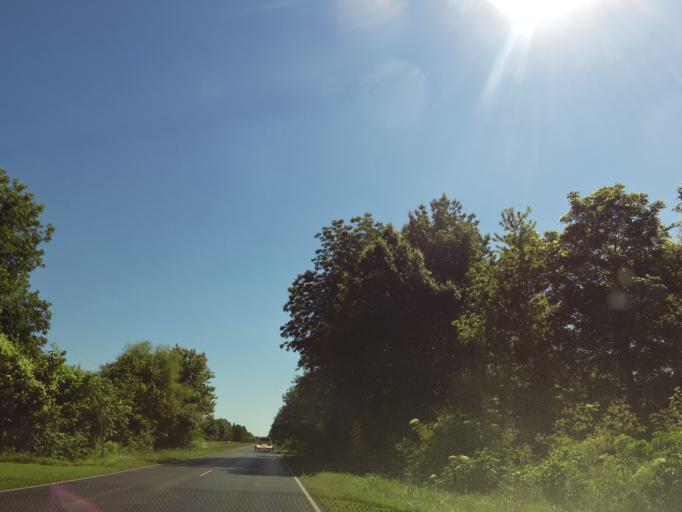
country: US
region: Missouri
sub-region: Dunklin County
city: Campbell
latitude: 36.4809
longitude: -90.0948
